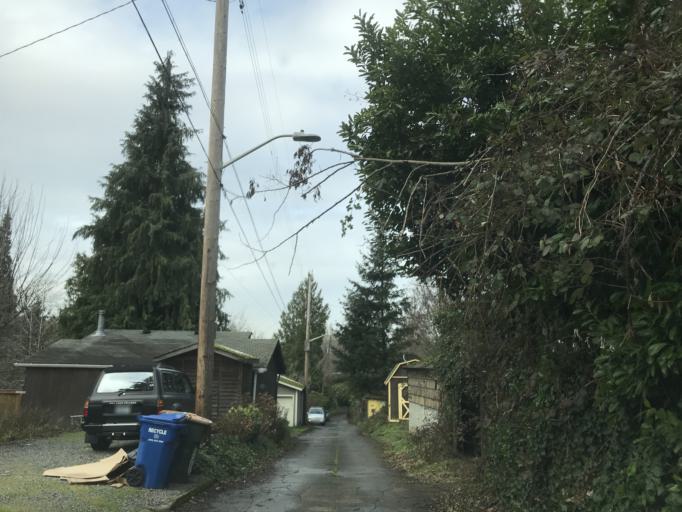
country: US
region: Washington
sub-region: King County
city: Seattle
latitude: 47.6384
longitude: -122.3051
